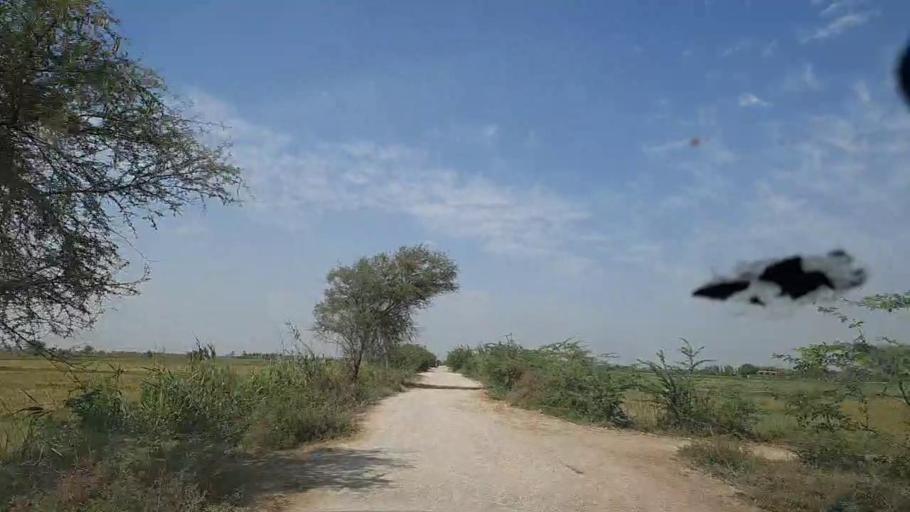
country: PK
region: Sindh
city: Daro Mehar
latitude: 24.6537
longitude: 68.0750
